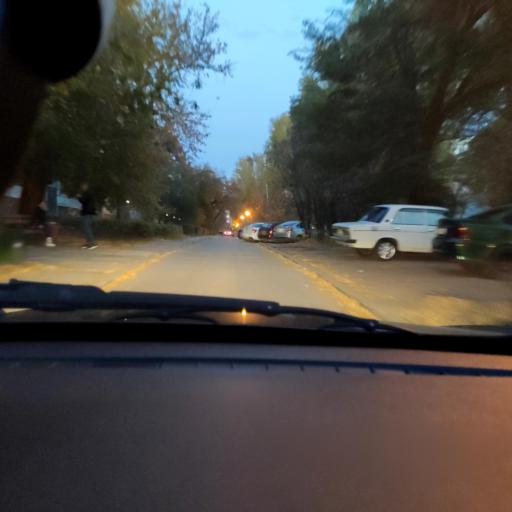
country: RU
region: Samara
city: Tol'yatti
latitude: 53.5323
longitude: 49.3000
